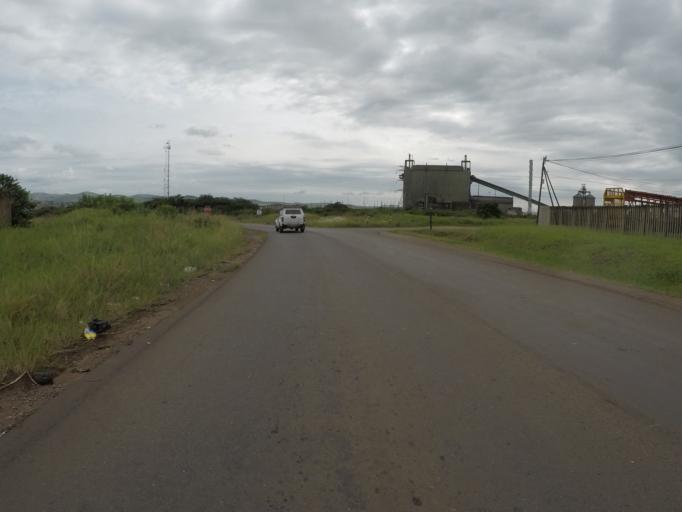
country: ZA
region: KwaZulu-Natal
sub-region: uThungulu District Municipality
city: Empangeni
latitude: -28.7243
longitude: 31.8669
